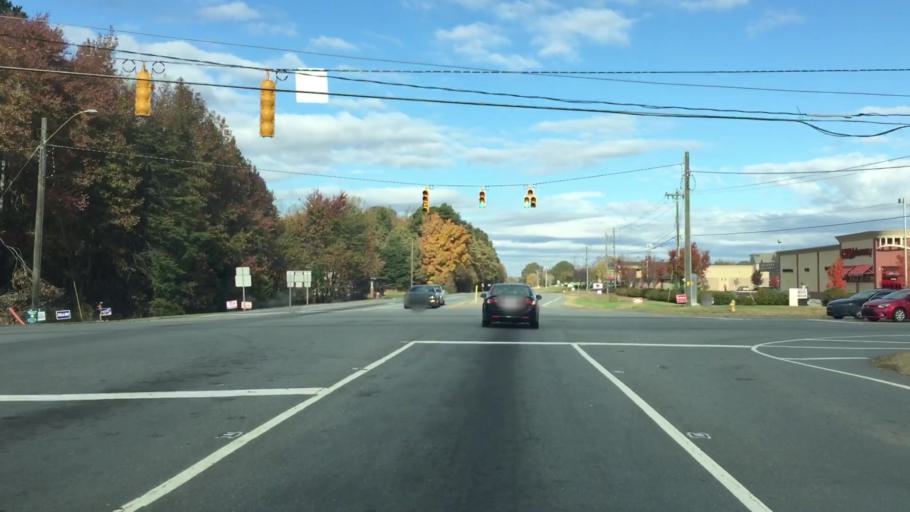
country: US
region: North Carolina
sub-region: Forsyth County
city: Walkertown
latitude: 36.1649
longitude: -80.1373
